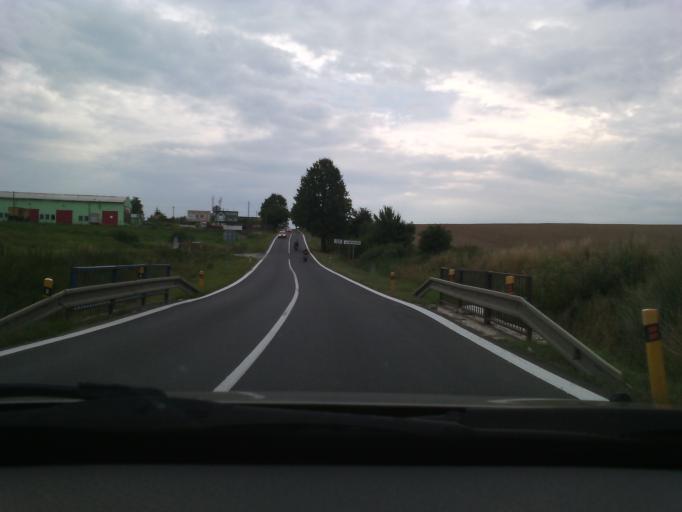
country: SK
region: Presovsky
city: Spisska Bela
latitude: 49.1963
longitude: 20.4647
